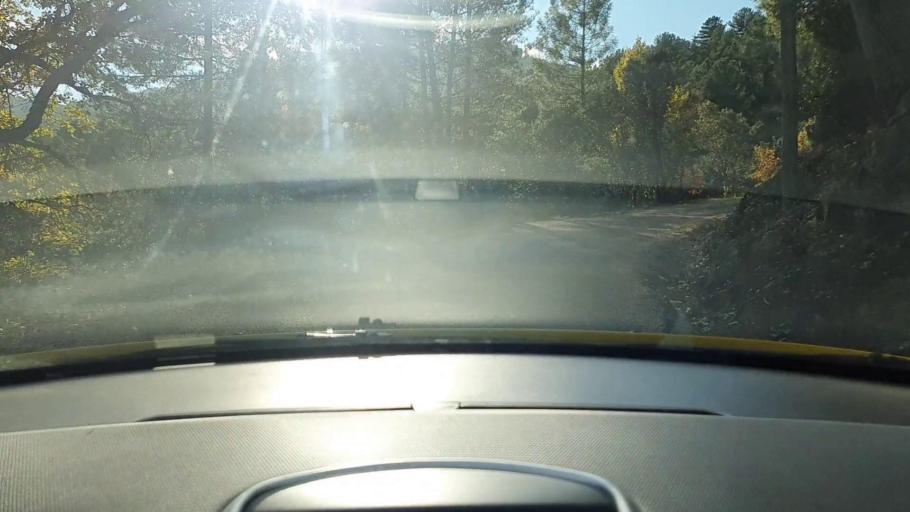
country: FR
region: Languedoc-Roussillon
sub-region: Departement du Gard
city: Branoux-les-Taillades
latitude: 44.2353
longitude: 3.9604
